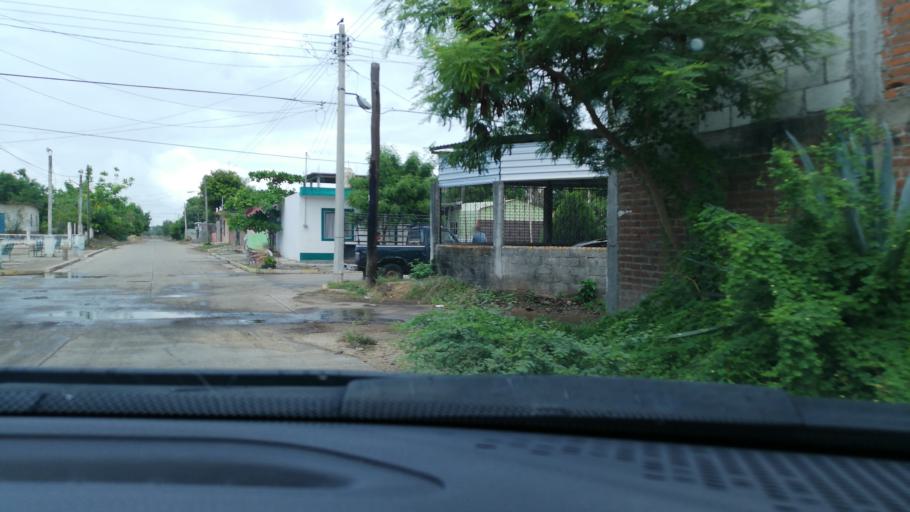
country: MX
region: Oaxaca
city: Asuncion Ixtaltepec
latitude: 16.5077
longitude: -95.0492
